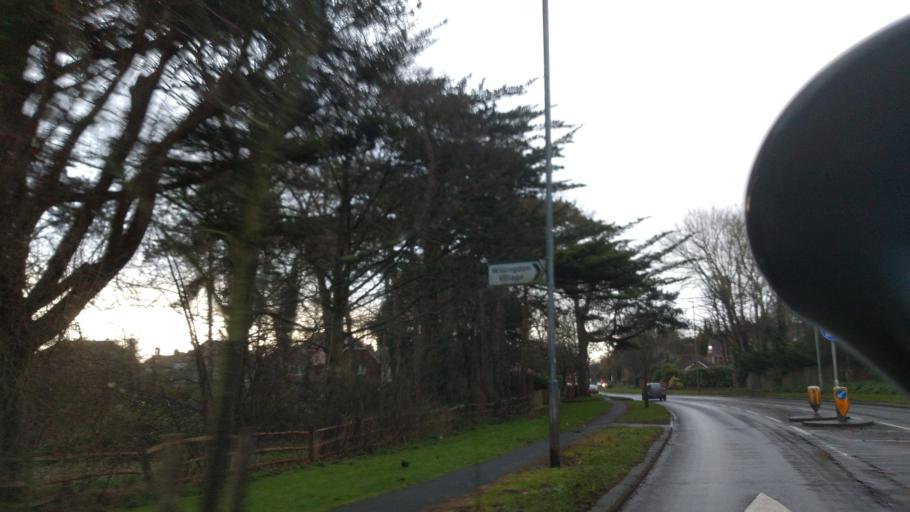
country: GB
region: England
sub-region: East Sussex
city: Eastbourne
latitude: 50.7929
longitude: 0.2562
